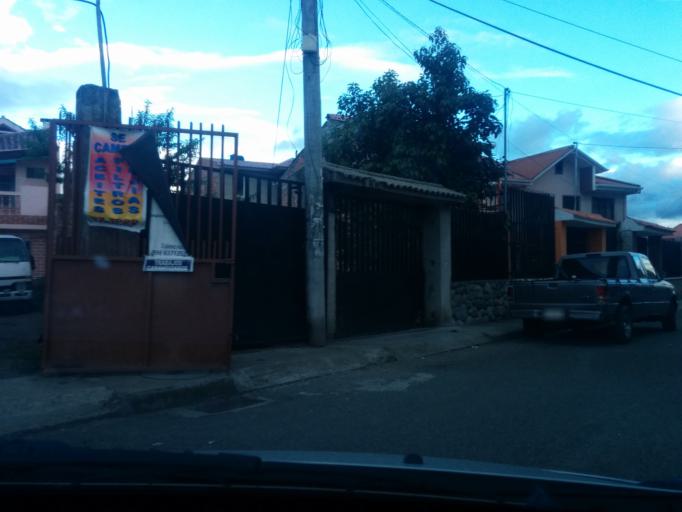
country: EC
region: Azuay
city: Cuenca
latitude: -2.8852
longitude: -78.9683
